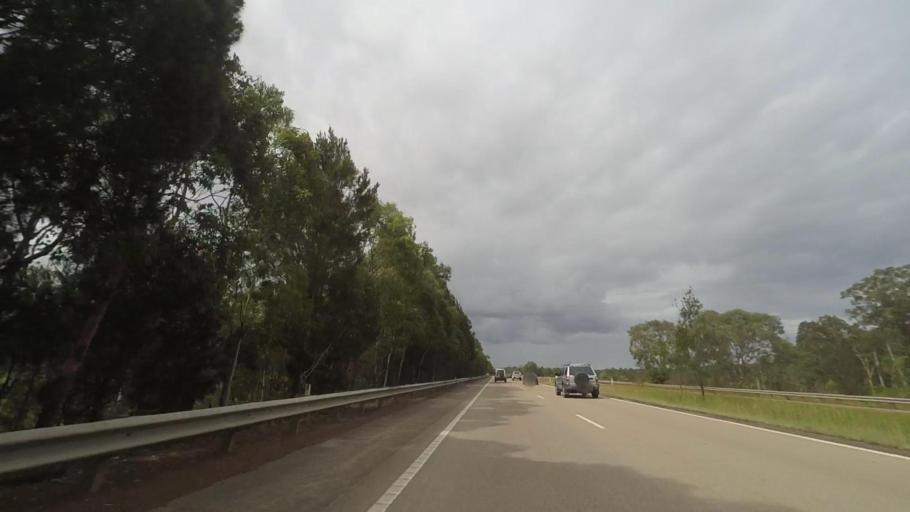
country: AU
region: New South Wales
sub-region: Port Stephens Shire
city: Raymond Terrace
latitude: -32.7336
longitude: 151.7813
